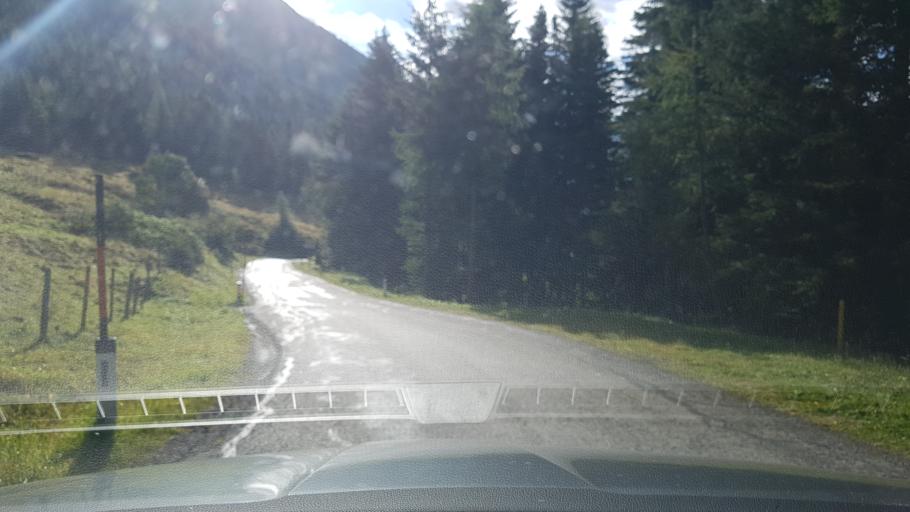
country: AT
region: Styria
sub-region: Politischer Bezirk Liezen
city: Sankt Nikolai im Solktal
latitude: 47.2525
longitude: 14.0791
